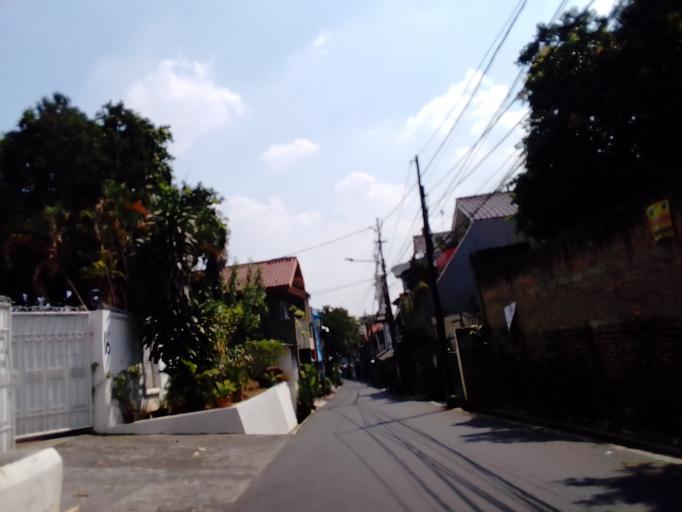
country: ID
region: Jakarta Raya
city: Jakarta
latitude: -6.2586
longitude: 106.8020
